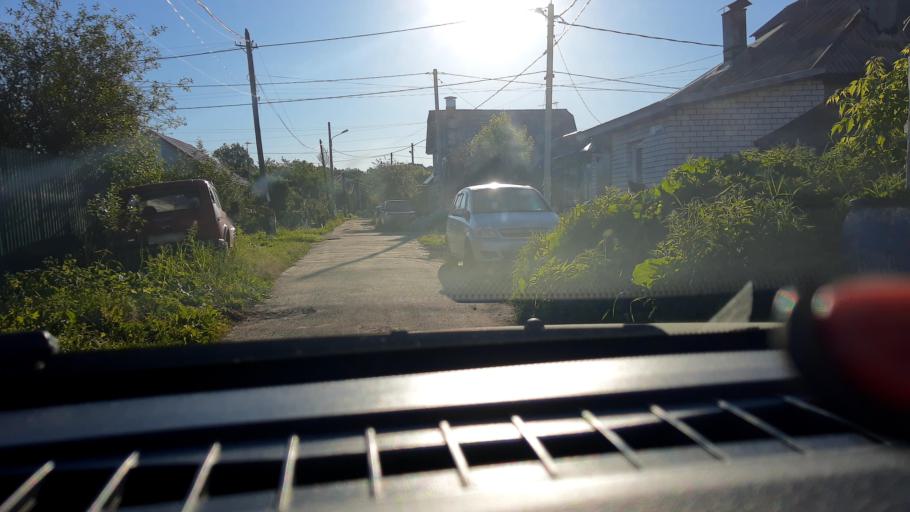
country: RU
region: Nizjnij Novgorod
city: Burevestnik
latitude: 56.2122
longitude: 43.8141
